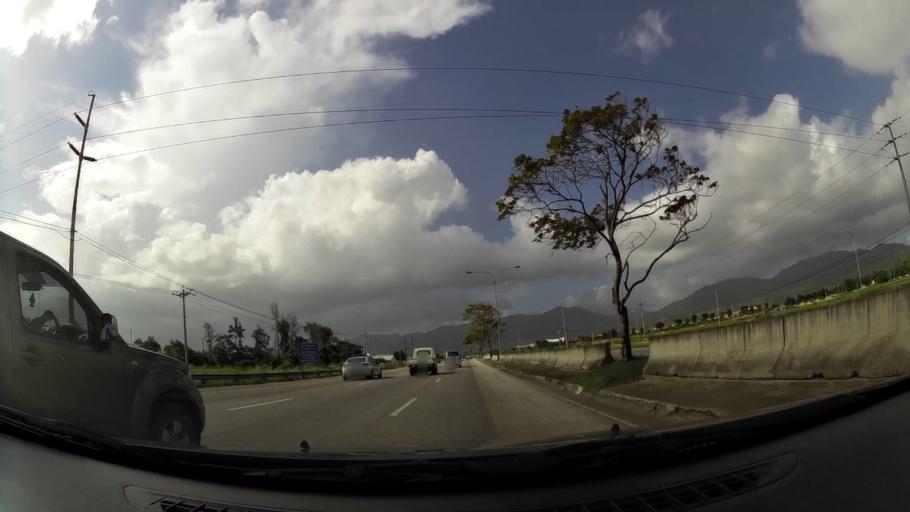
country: TT
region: Tunapuna/Piarco
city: Arouca
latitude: 10.6197
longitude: -61.3524
